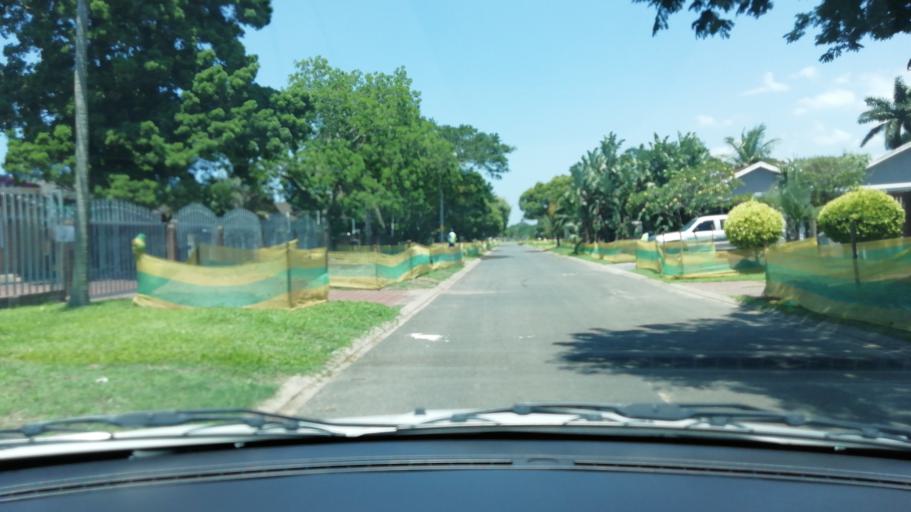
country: ZA
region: KwaZulu-Natal
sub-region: uThungulu District Municipality
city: Richards Bay
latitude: -28.7339
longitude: 32.0606
